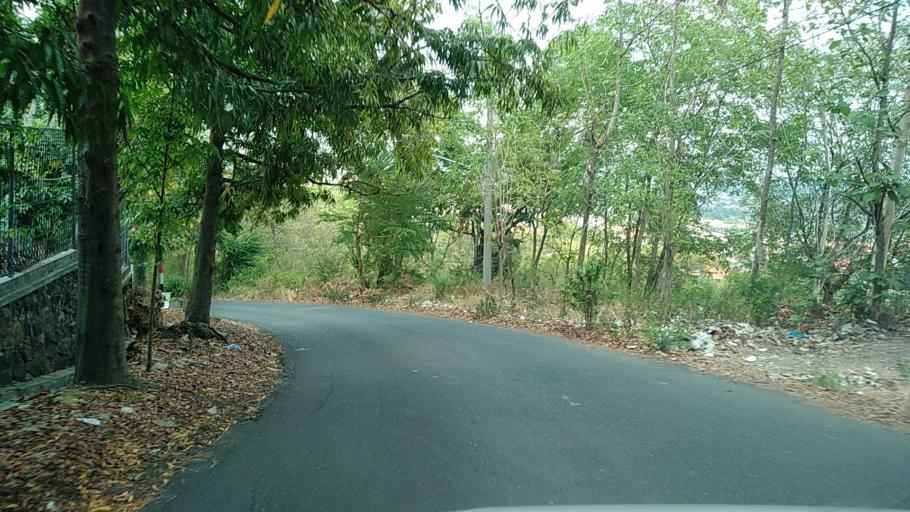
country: ID
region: Central Java
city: Semarang
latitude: -7.0164
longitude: 110.3991
